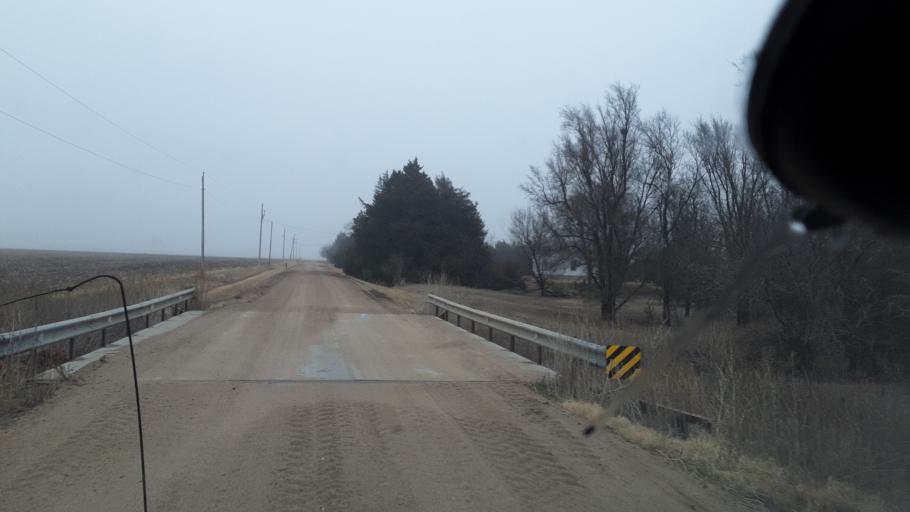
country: US
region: Kansas
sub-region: Reno County
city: South Hutchinson
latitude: 37.9842
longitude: -97.9742
